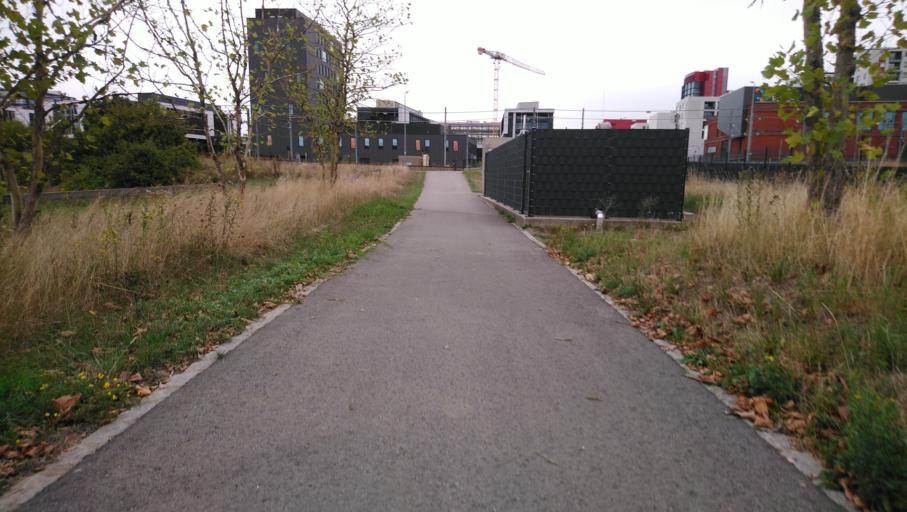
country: LU
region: Luxembourg
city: Belvaux
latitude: 49.4998
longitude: 5.9431
